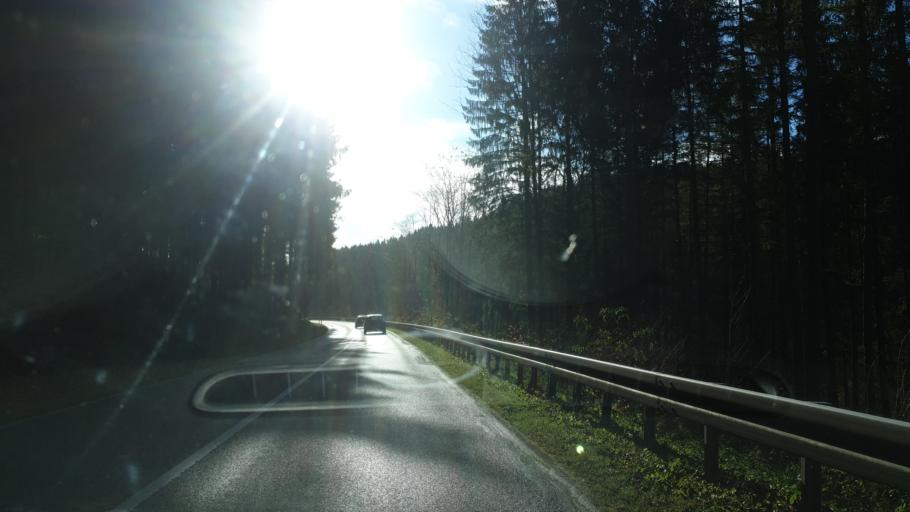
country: DE
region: Saxony
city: Bockau
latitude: 50.5636
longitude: 12.6914
